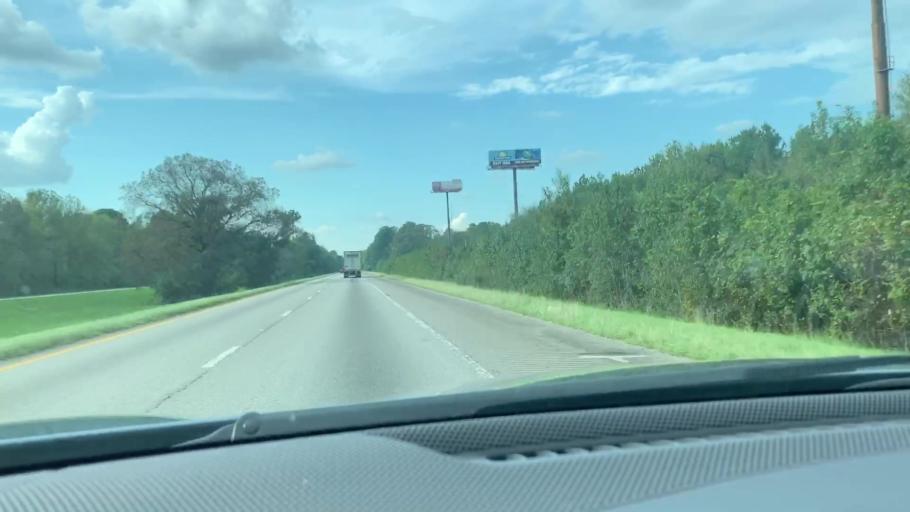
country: US
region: South Carolina
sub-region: Dorchester County
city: Saint George
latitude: 33.3521
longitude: -80.5837
